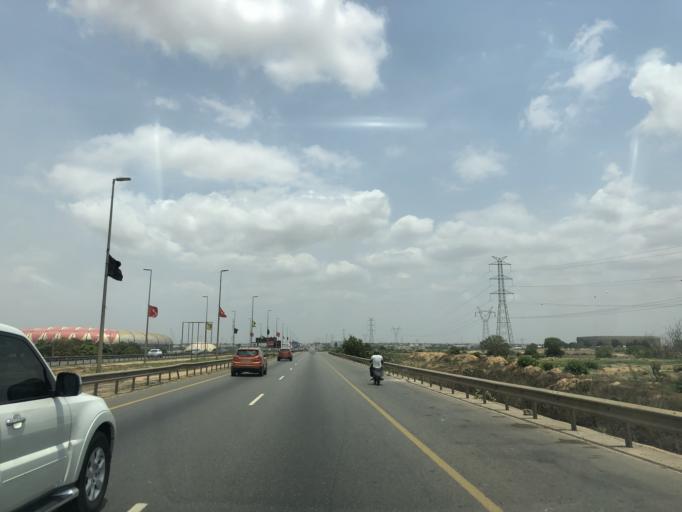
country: AO
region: Luanda
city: Luanda
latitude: -8.9732
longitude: 13.2731
